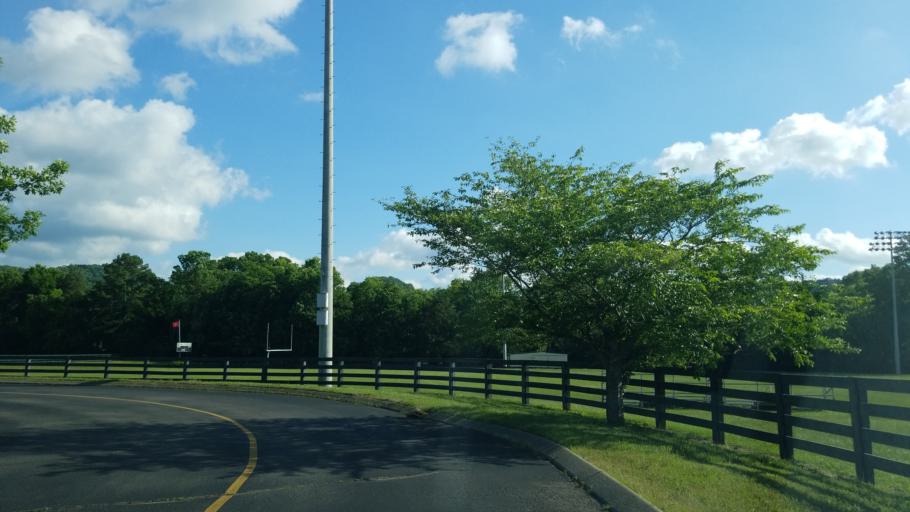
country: US
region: Tennessee
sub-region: Davidson County
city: Forest Hills
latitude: 36.0322
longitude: -86.8609
